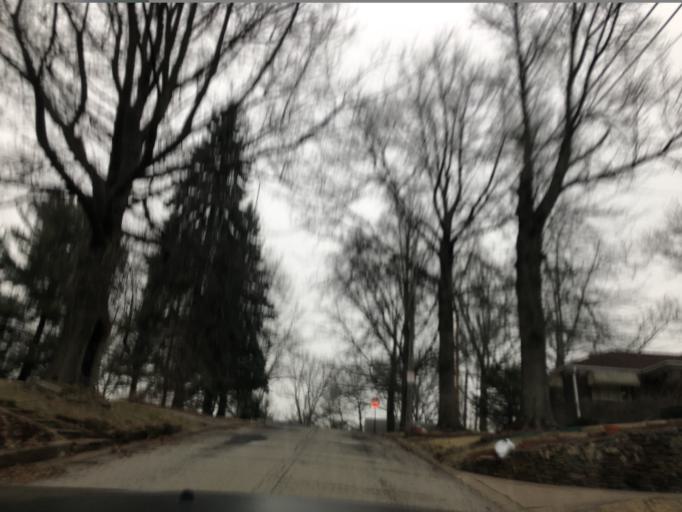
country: US
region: Pennsylvania
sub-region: Allegheny County
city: Wilkinsburg
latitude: 40.4575
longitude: -79.8618
